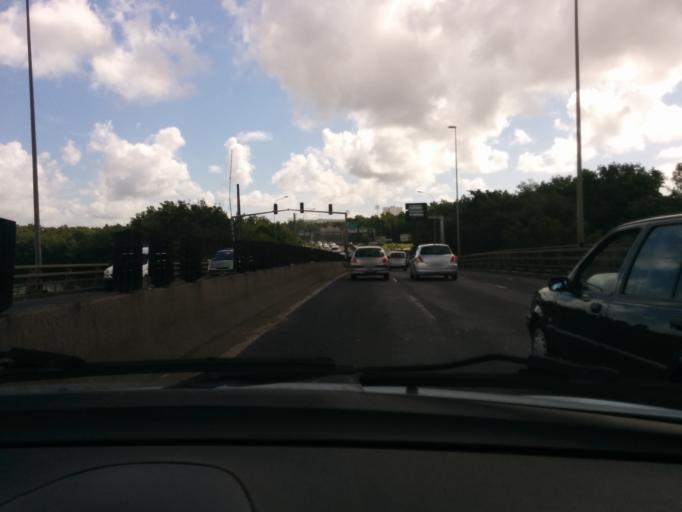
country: GP
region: Guadeloupe
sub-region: Guadeloupe
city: Pointe-a-Pitre
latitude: 16.2535
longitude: -61.5486
